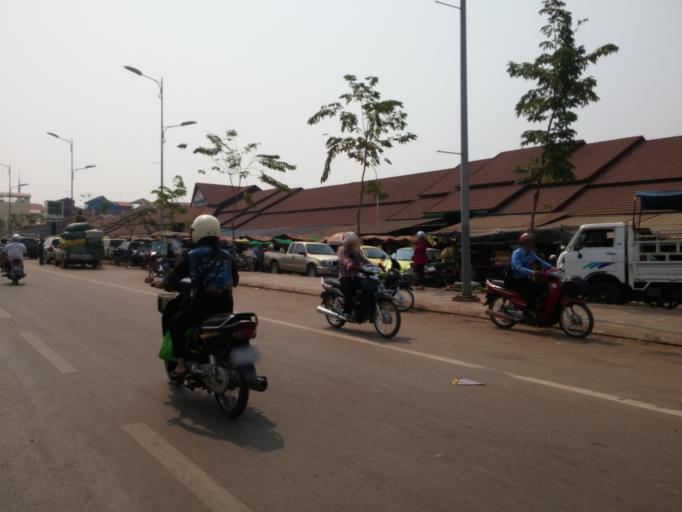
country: KH
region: Siem Reap
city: Siem Reap
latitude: 13.3604
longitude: 103.8739
